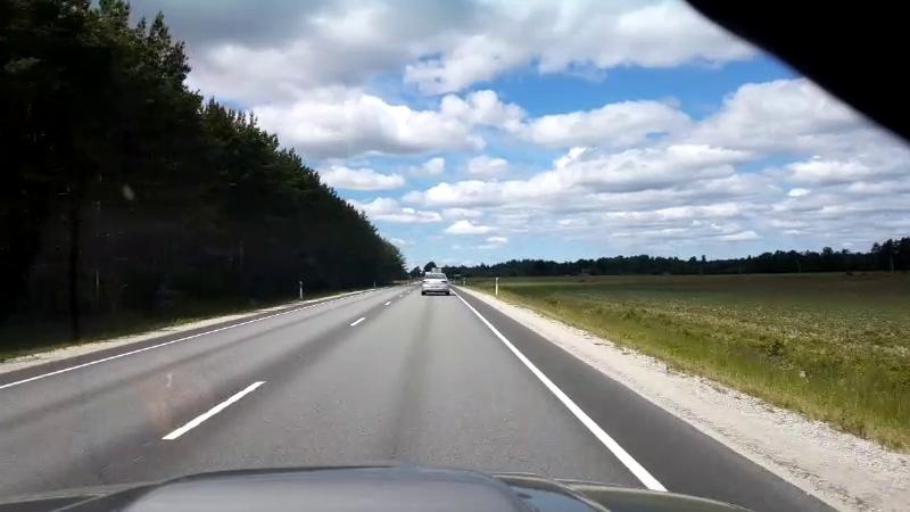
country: EE
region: Paernumaa
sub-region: Halinga vald
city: Parnu-Jaagupi
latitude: 58.6653
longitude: 24.4599
